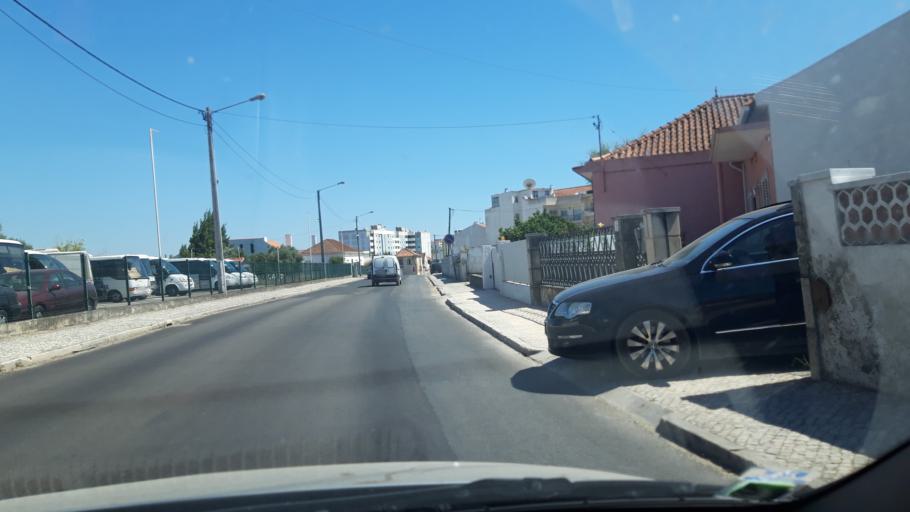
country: PT
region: Santarem
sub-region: Entroncamento
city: Entroncamento
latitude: 39.4650
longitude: -8.4643
